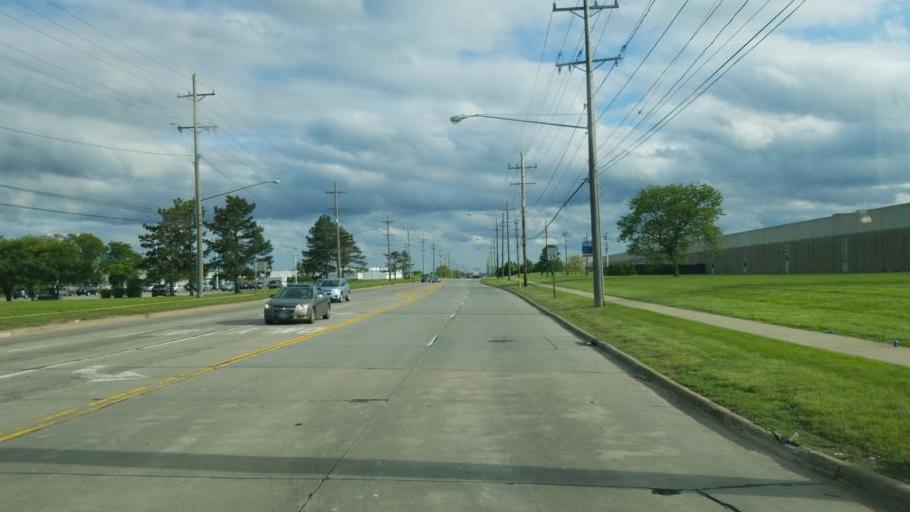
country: US
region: Ohio
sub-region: Cuyahoga County
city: Solon
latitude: 41.3870
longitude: -81.4692
